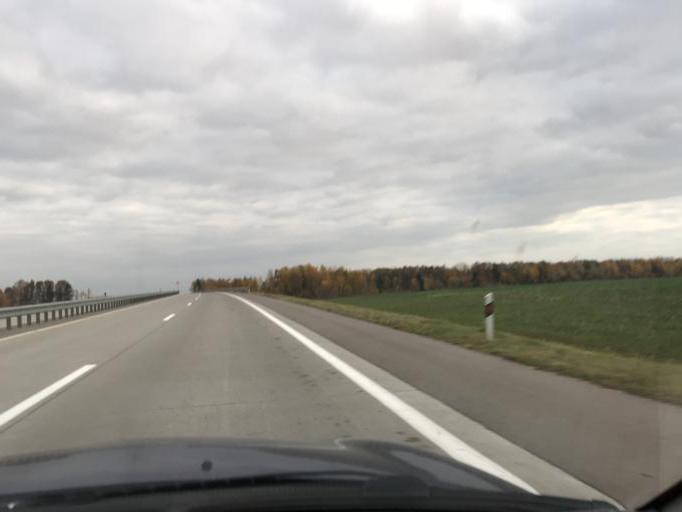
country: BY
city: Fanipol
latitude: 53.7694
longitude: 27.3643
